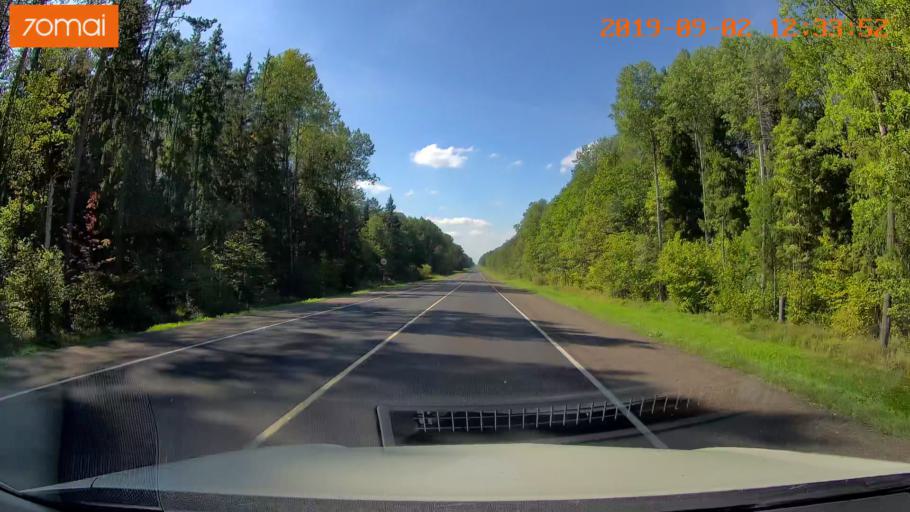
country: RU
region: Smolensk
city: Shumyachi
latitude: 53.8146
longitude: 32.4182
